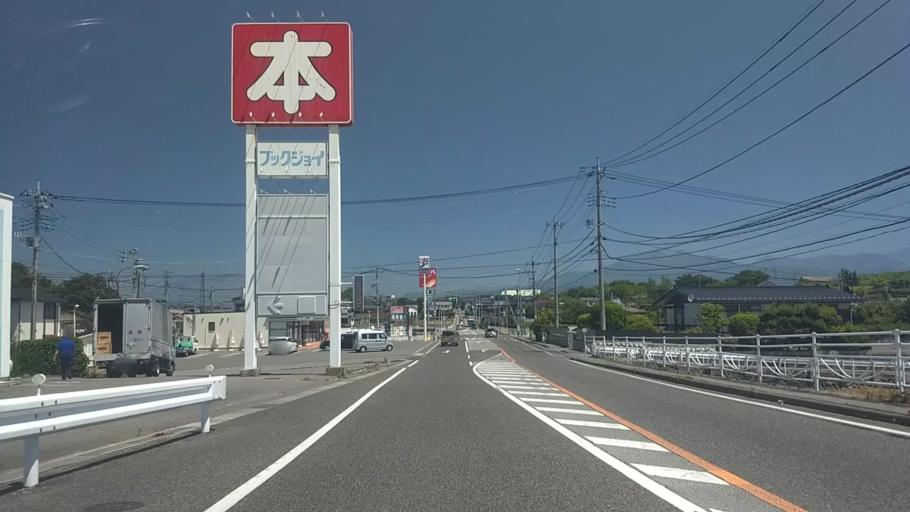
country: JP
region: Yamanashi
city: Nirasaki
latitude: 35.6732
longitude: 138.4649
